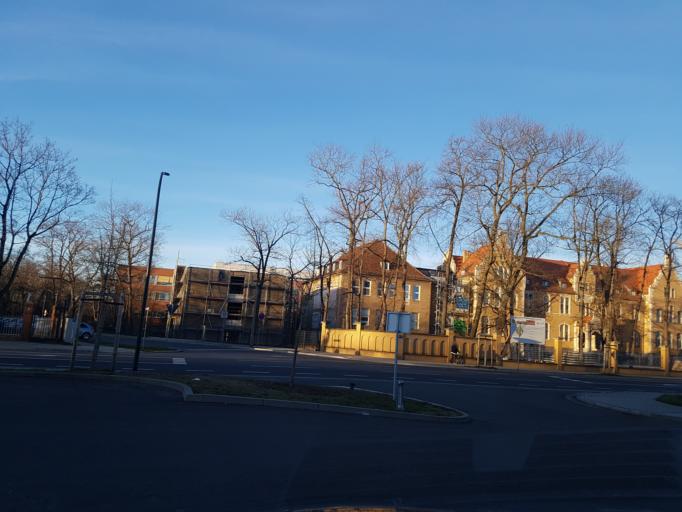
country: DE
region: Brandenburg
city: Finsterwalde
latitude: 51.6344
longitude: 13.6979
